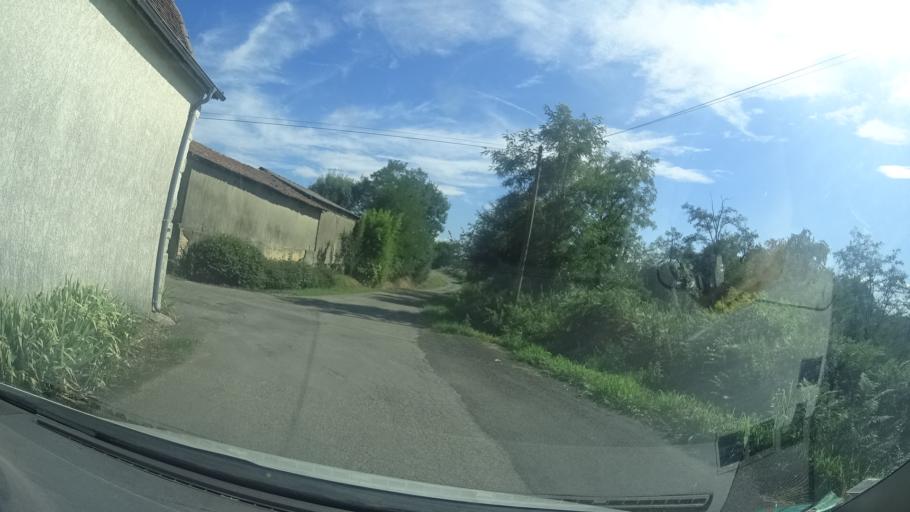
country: FR
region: Aquitaine
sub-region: Departement des Pyrenees-Atlantiques
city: Mont
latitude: 43.5014
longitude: -0.6760
